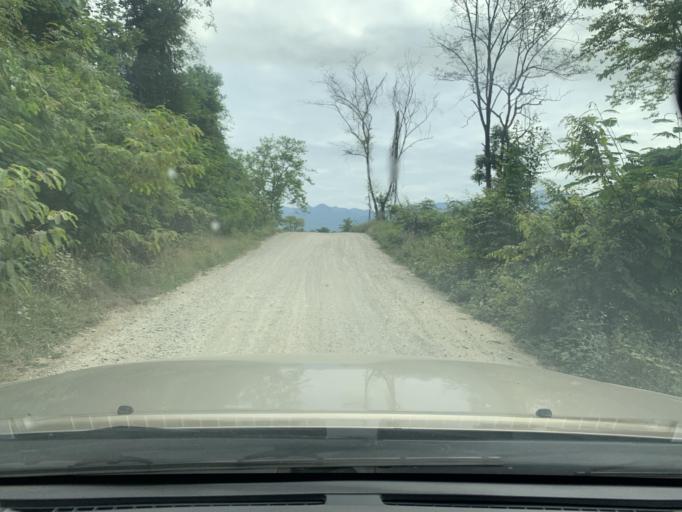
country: LA
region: Louangphabang
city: Louangphabang
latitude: 19.8863
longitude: 102.1886
